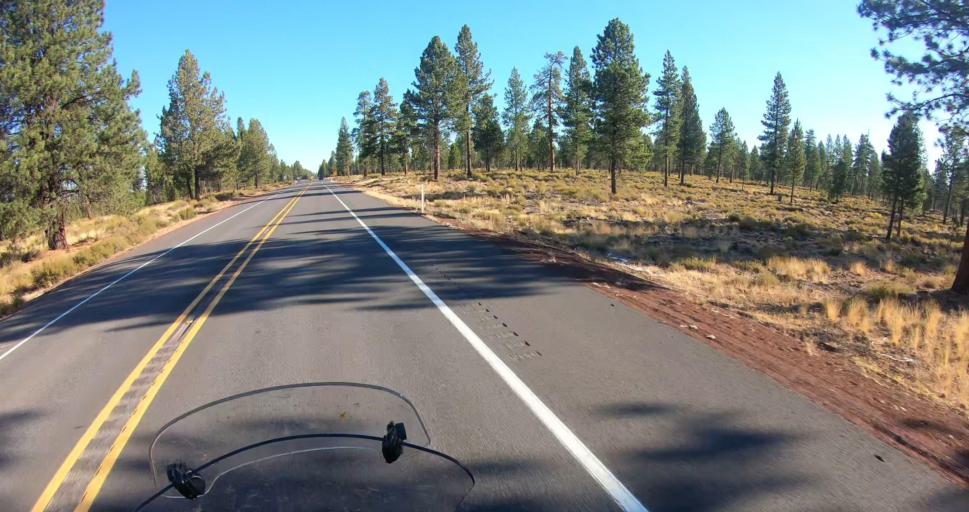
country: US
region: Oregon
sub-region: Deschutes County
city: Three Rivers
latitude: 43.7634
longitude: -121.4542
